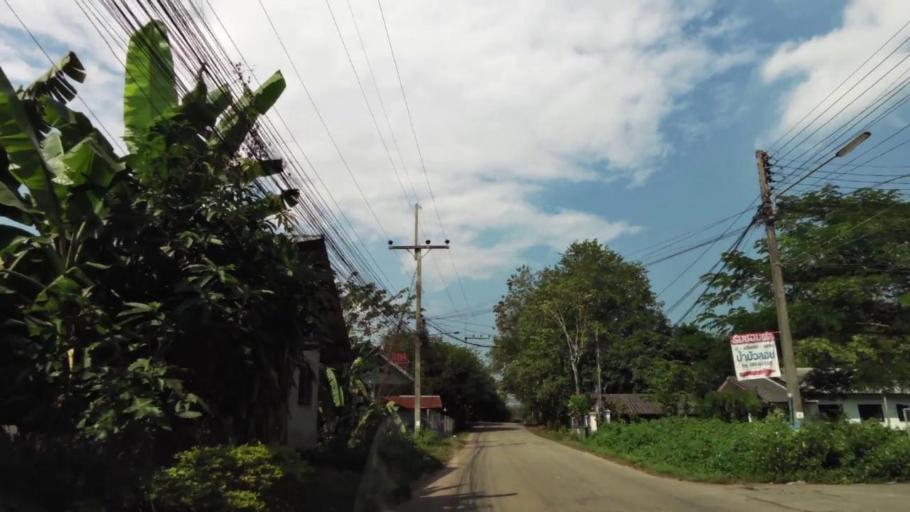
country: TH
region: Chiang Rai
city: Chiang Rai
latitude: 19.8882
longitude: 99.8035
